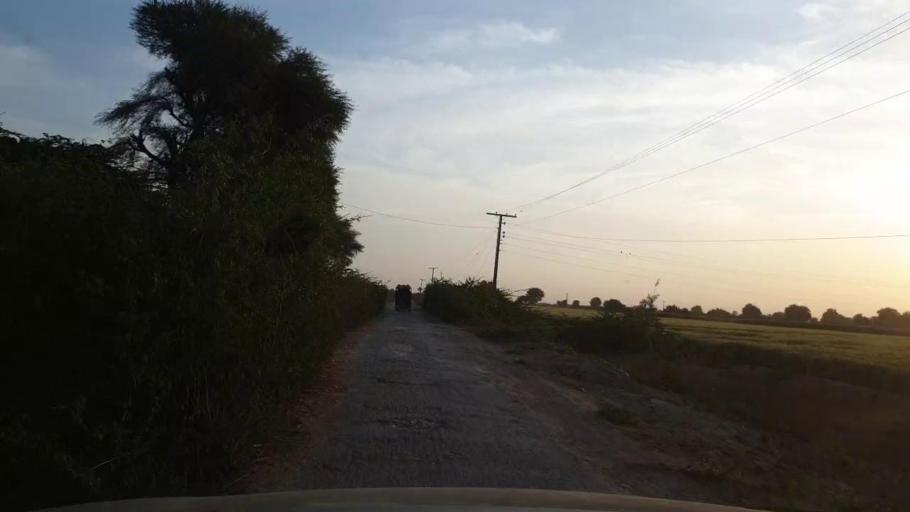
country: PK
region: Sindh
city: Kunri
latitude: 25.1395
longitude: 69.5778
